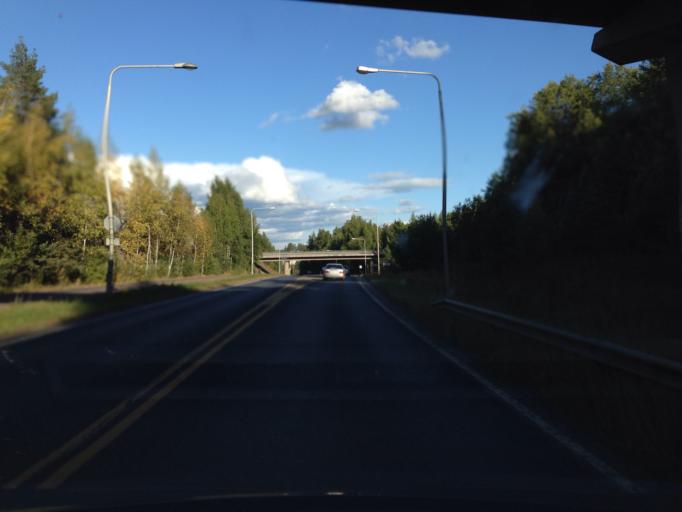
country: FI
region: Uusimaa
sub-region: Helsinki
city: Vantaa
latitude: 60.3469
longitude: 25.0633
